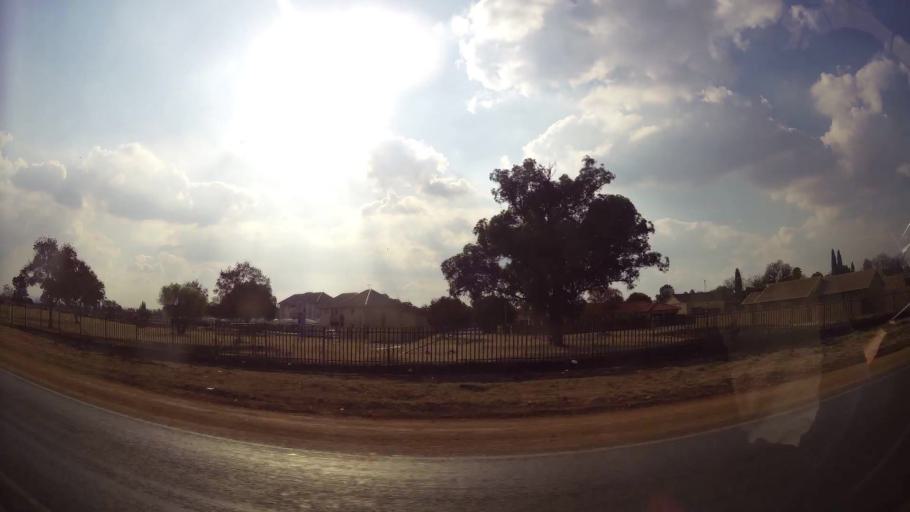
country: ZA
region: Gauteng
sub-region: Ekurhuleni Metropolitan Municipality
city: Boksburg
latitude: -26.2876
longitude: 28.2378
